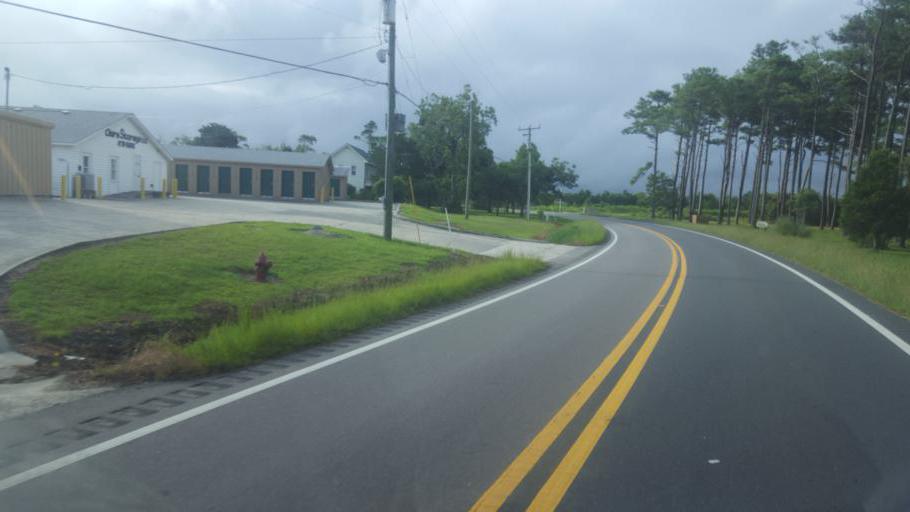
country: US
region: North Carolina
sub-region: Dare County
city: Manteo
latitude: 35.8800
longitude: -75.6596
